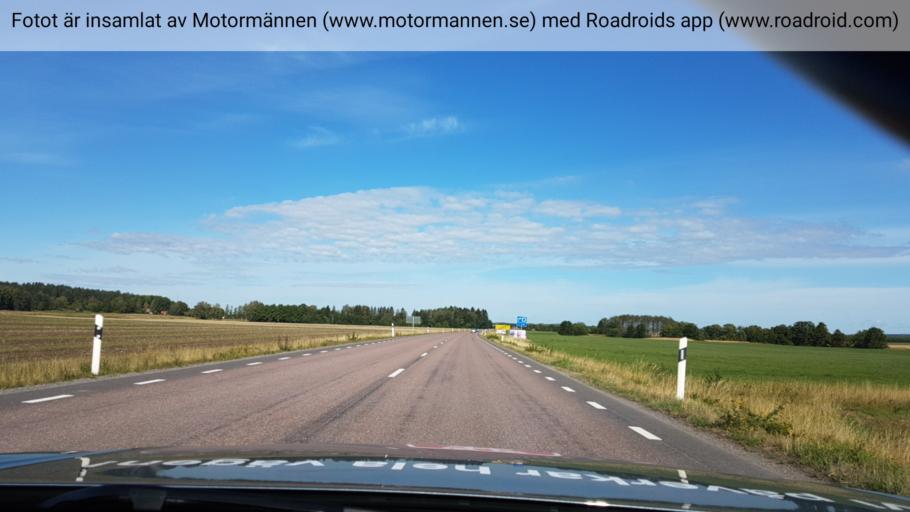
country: SE
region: Uppsala
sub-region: Uppsala Kommun
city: Gamla Uppsala
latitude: 59.8904
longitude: 17.5573
